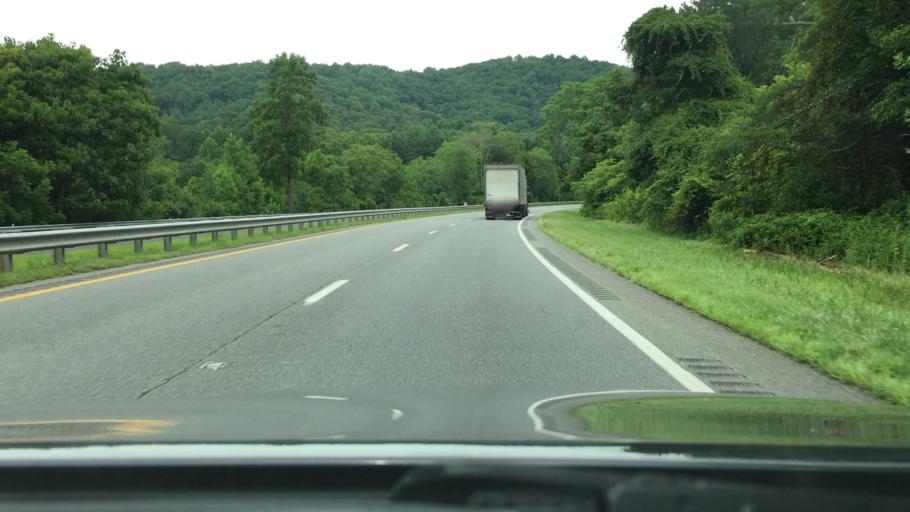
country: US
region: Virginia
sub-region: City of Charlottesville
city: Charlottesville
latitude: 38.0035
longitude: -78.5797
